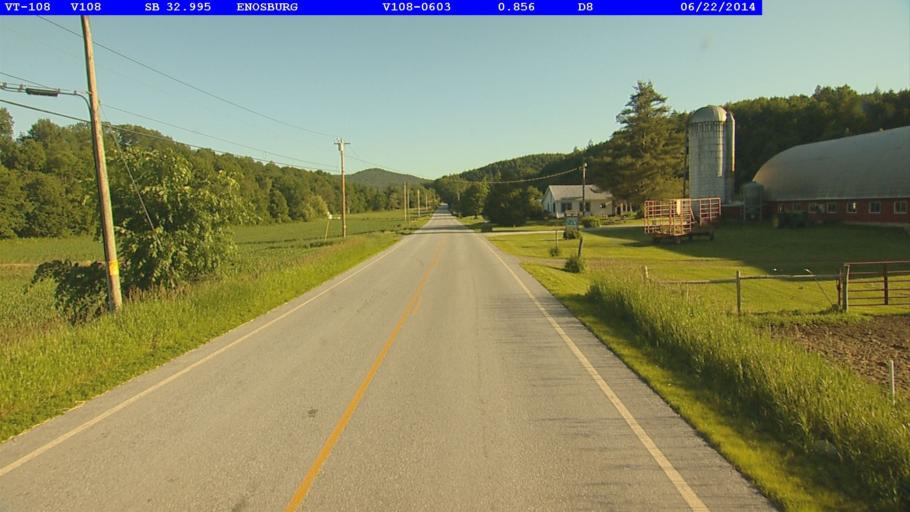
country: US
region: Vermont
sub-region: Franklin County
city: Enosburg Falls
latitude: 44.8503
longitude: -72.8051
